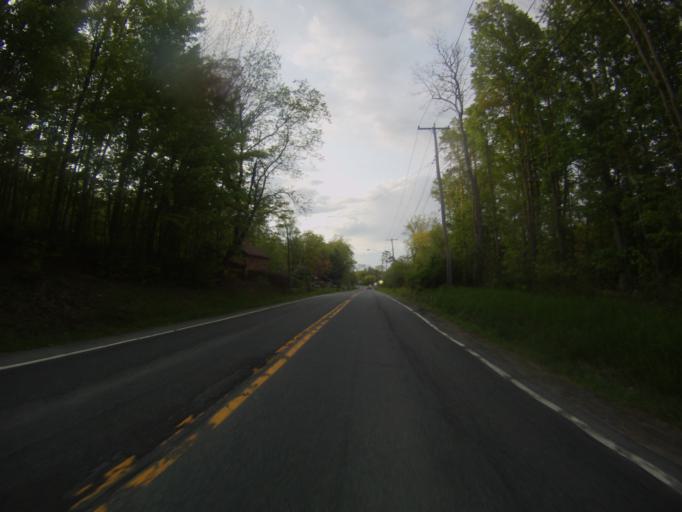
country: US
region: New York
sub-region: Essex County
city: Ticonderoga
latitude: 43.9451
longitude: -73.4177
